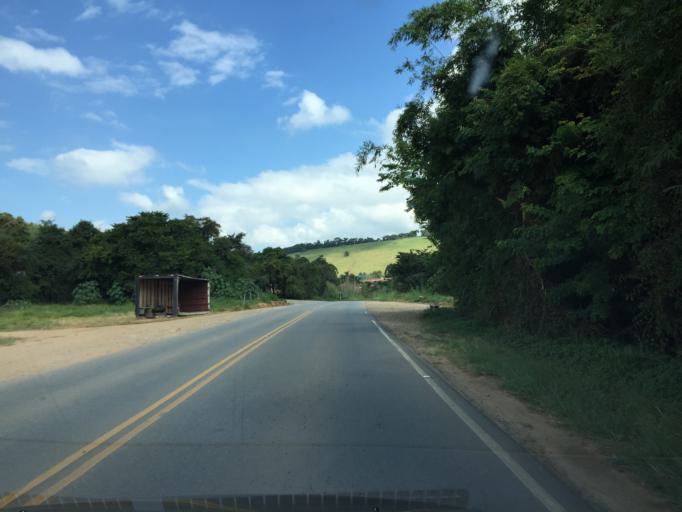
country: BR
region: Minas Gerais
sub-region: Passa Quatro
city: Passa Quatro
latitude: -22.3625
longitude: -44.9529
